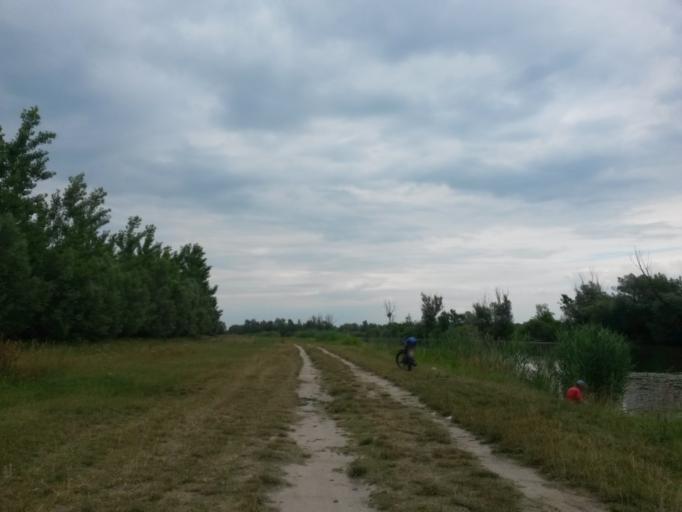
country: HR
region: Osjecko-Baranjska
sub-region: Grad Osijek
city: Bilje
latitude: 45.5894
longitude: 18.7564
